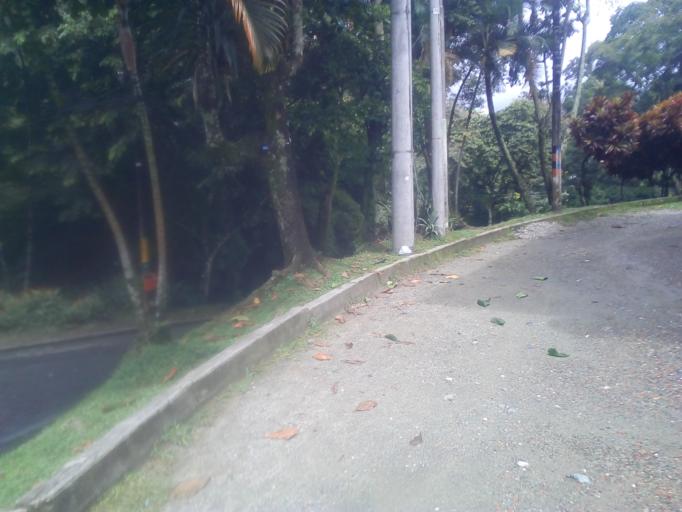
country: CO
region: Tolima
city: Ibague
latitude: 4.4472
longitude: -75.2418
